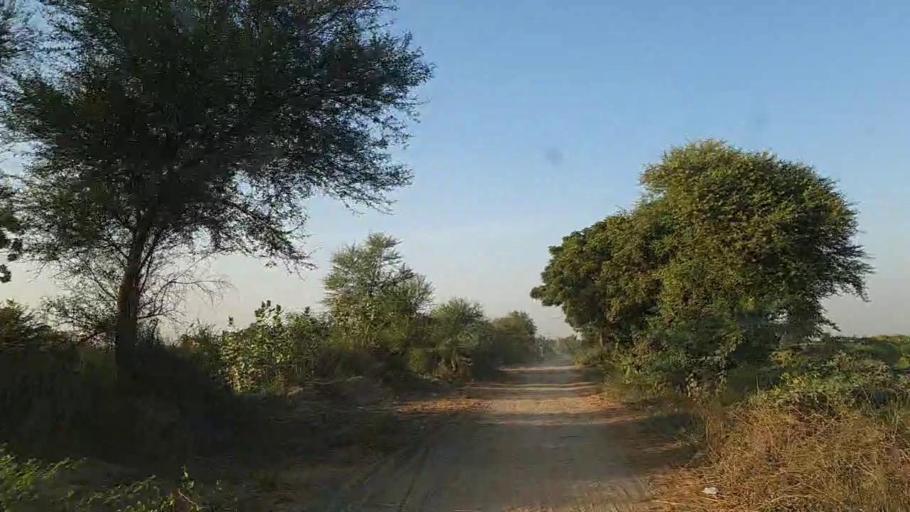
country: PK
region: Sindh
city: Mirpur Batoro
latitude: 24.7202
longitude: 68.2140
